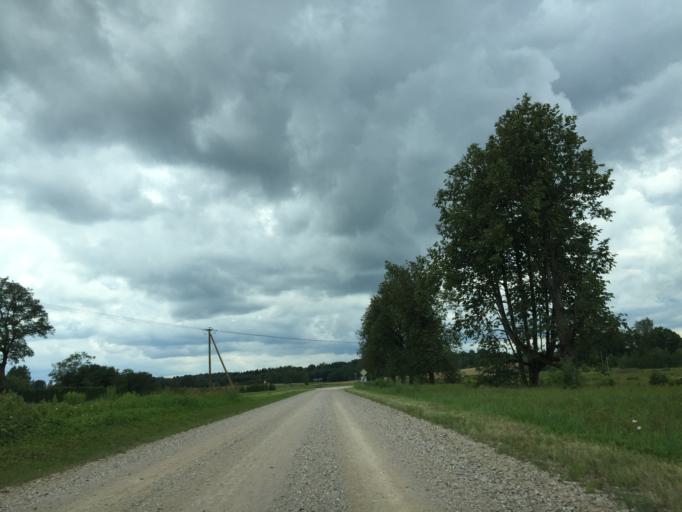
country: LV
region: Malpils
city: Malpils
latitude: 56.8603
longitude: 25.0202
